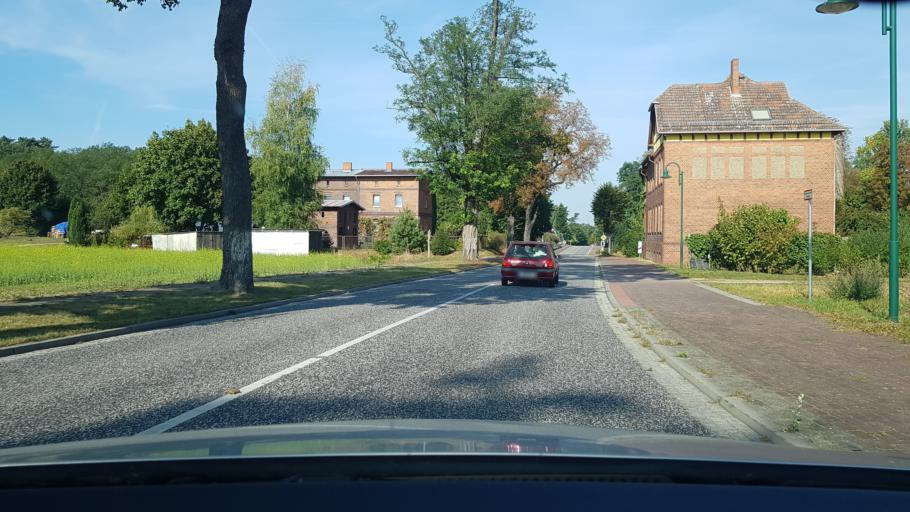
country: DE
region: Brandenburg
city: Mixdorf
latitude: 52.1633
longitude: 14.3803
